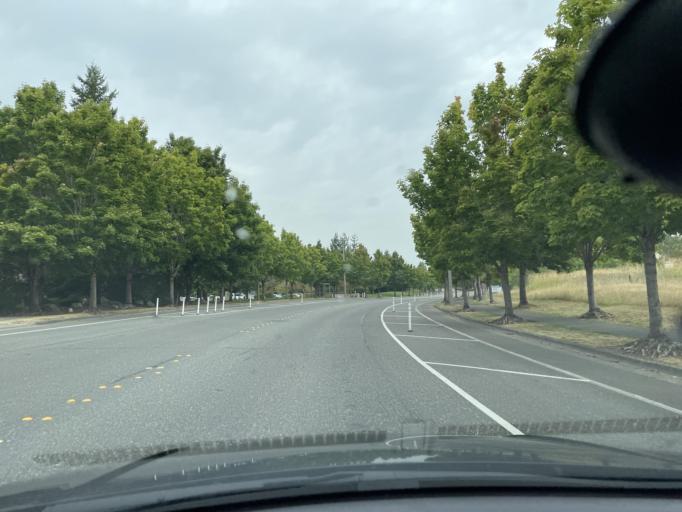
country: US
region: Washington
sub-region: Whatcom County
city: Bellingham
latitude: 48.8073
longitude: -122.4979
